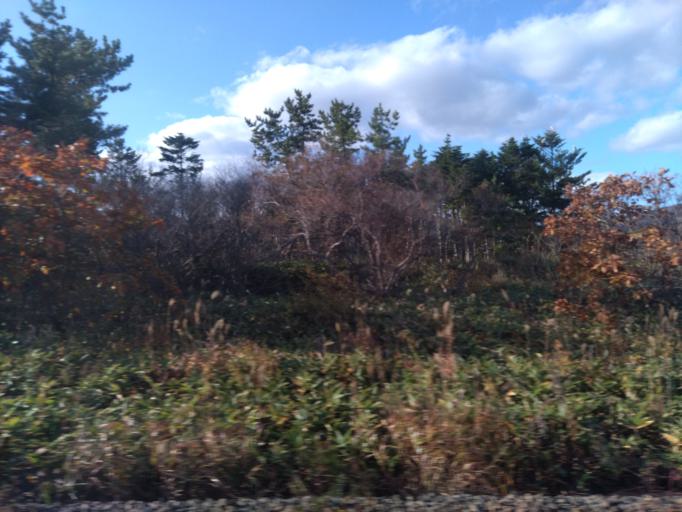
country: JP
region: Hokkaido
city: Niseko Town
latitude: 42.5805
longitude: 140.4555
